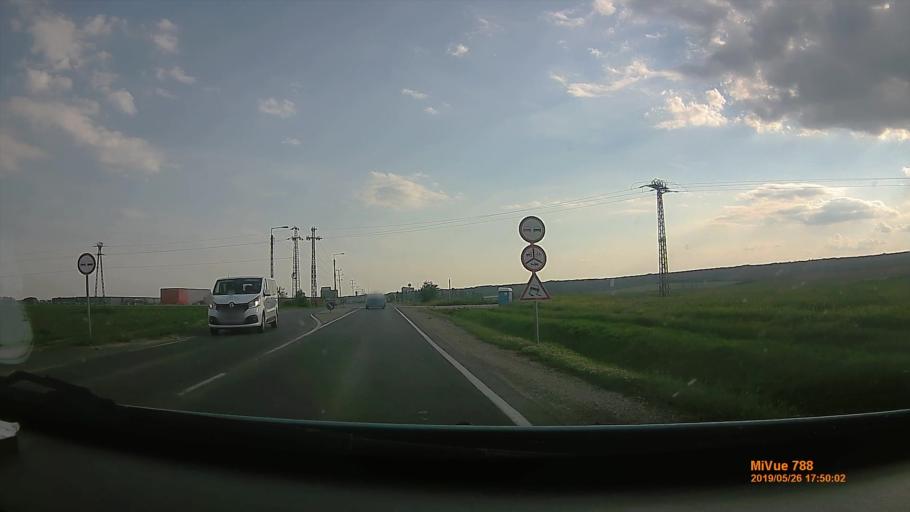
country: HU
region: Borsod-Abauj-Zemplen
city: Szikszo
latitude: 48.1854
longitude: 20.9221
